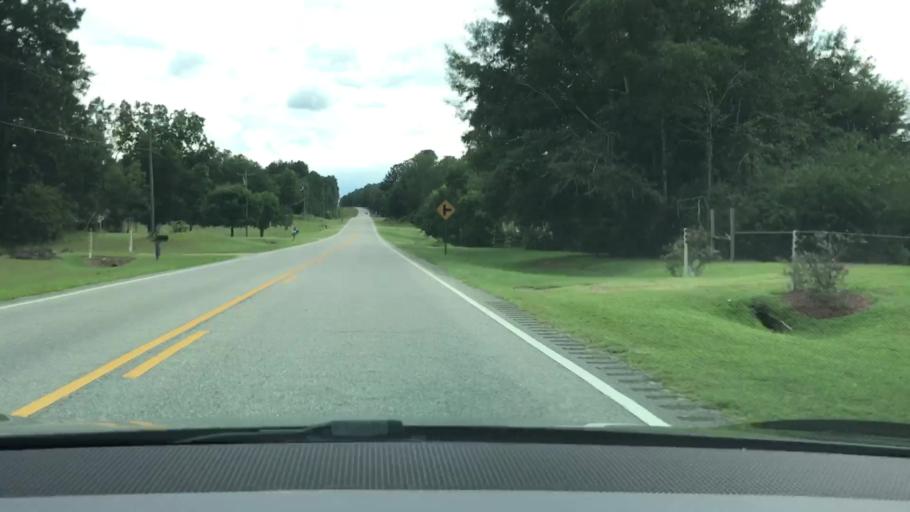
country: US
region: Alabama
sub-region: Pike County
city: Troy
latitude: 31.6476
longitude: -85.9697
